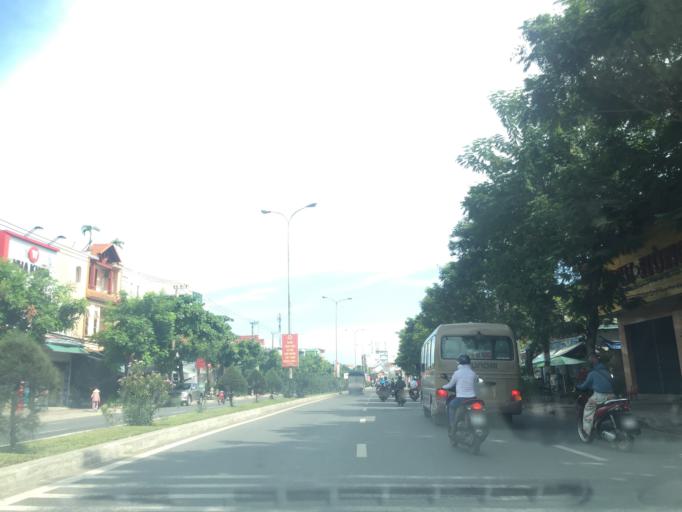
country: VN
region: Da Nang
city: Lien Chieu
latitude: 16.0585
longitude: 108.1652
